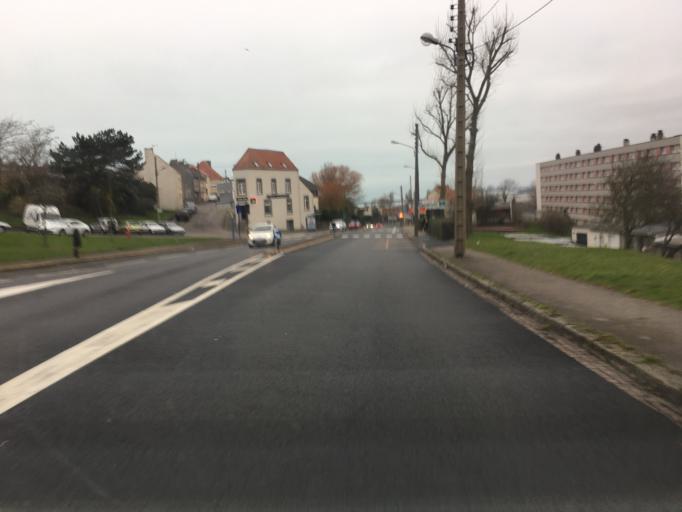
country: FR
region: Nord-Pas-de-Calais
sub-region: Departement du Pas-de-Calais
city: Outreau
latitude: 50.7162
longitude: 1.5911
